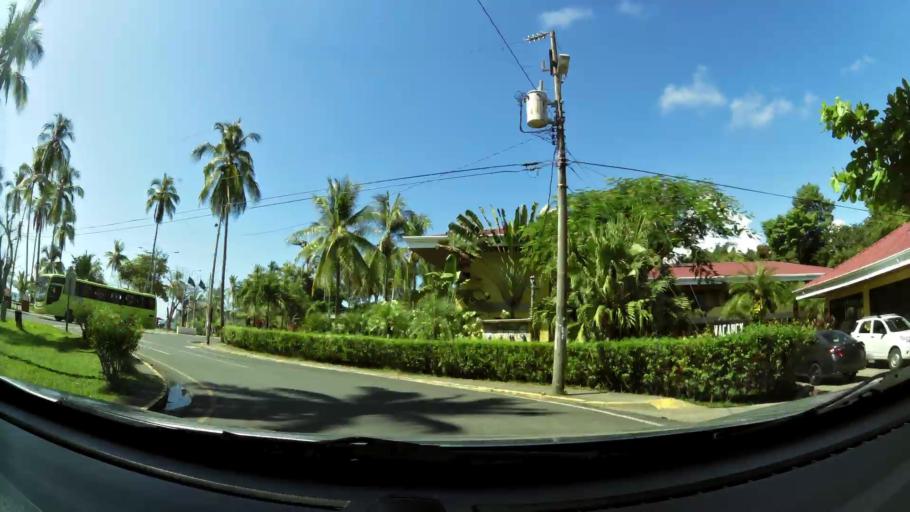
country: CR
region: Puntarenas
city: Quepos
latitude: 9.3897
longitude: -84.1472
